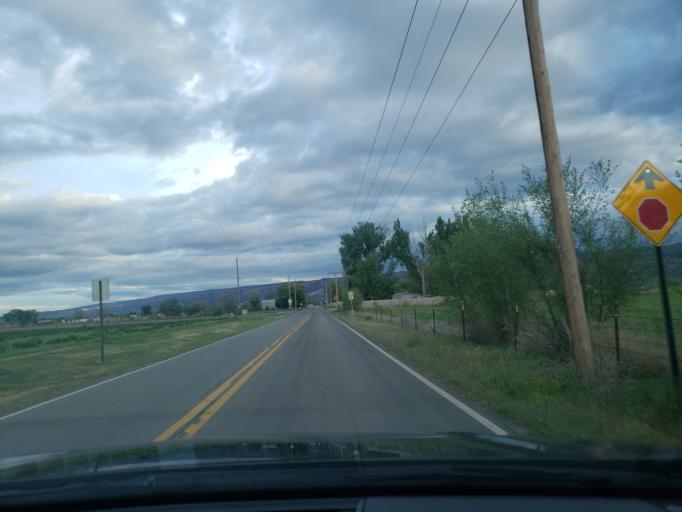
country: US
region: Colorado
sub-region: Mesa County
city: Fruita
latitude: 39.1655
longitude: -108.7012
